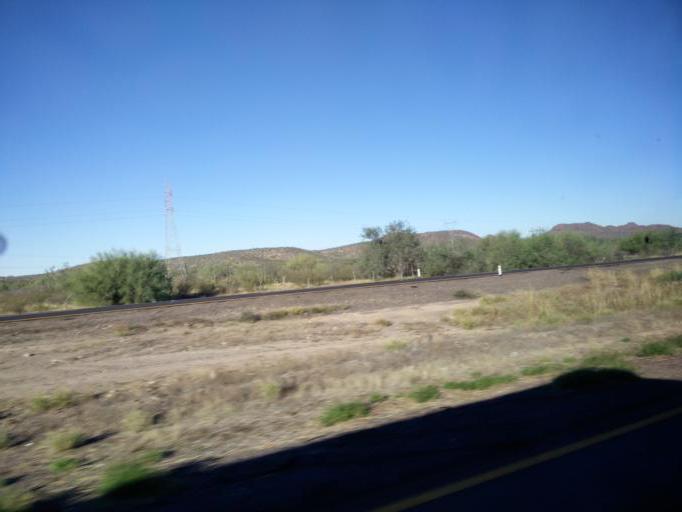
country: MX
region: Sonora
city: Heroica Guaymas
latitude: 28.2578
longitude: -111.0297
